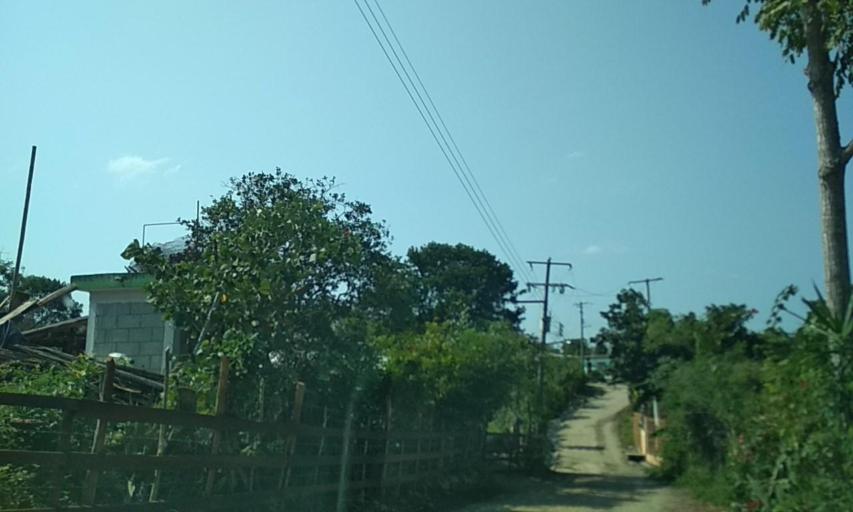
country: MX
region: Veracruz
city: Gutierrez Zamora
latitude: 20.3764
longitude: -97.1478
